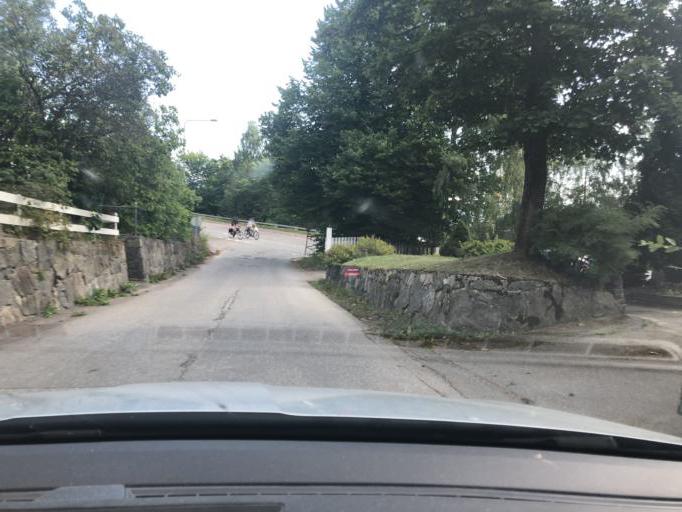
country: SE
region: Vaesternorrland
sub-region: Sundsvalls Kommun
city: Sundsvall
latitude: 62.3965
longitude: 17.3245
